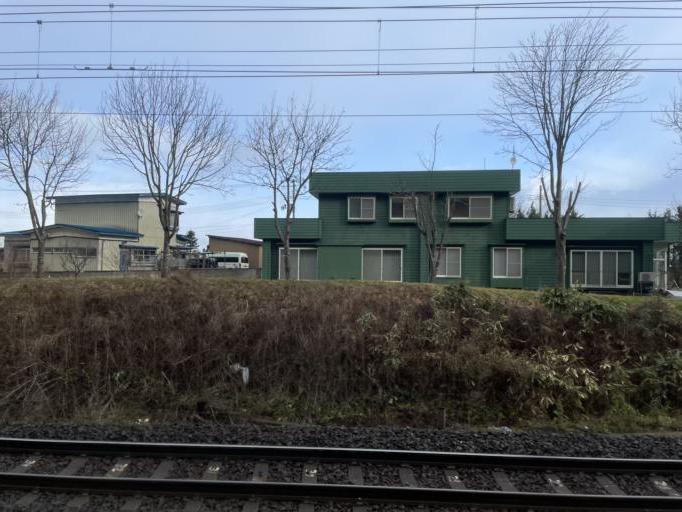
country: JP
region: Aomori
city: Aomori Shi
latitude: 40.9230
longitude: 141.0224
